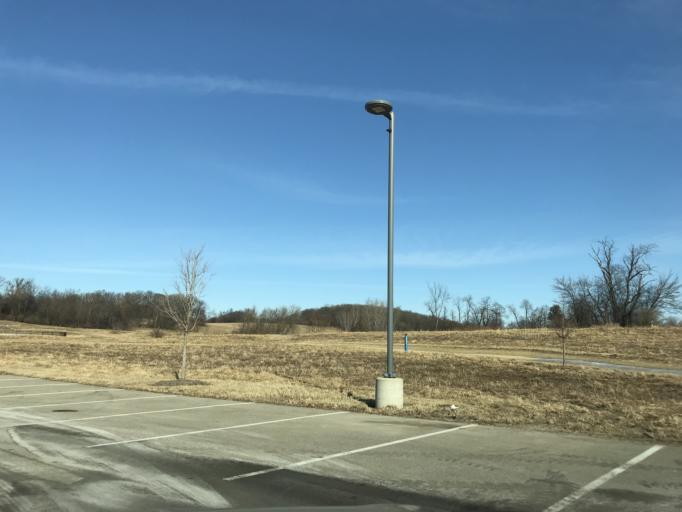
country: US
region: Wisconsin
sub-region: Dane County
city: Windsor
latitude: 43.1545
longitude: -89.2981
